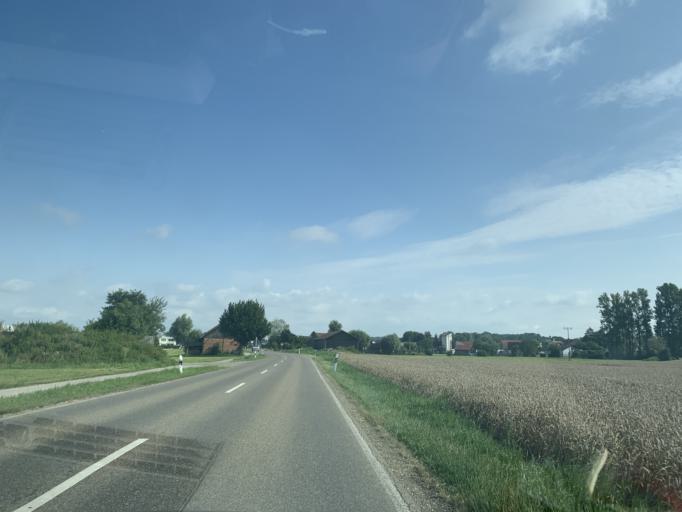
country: DE
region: Bavaria
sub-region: Swabia
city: Kissing
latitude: 48.2926
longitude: 10.9819
